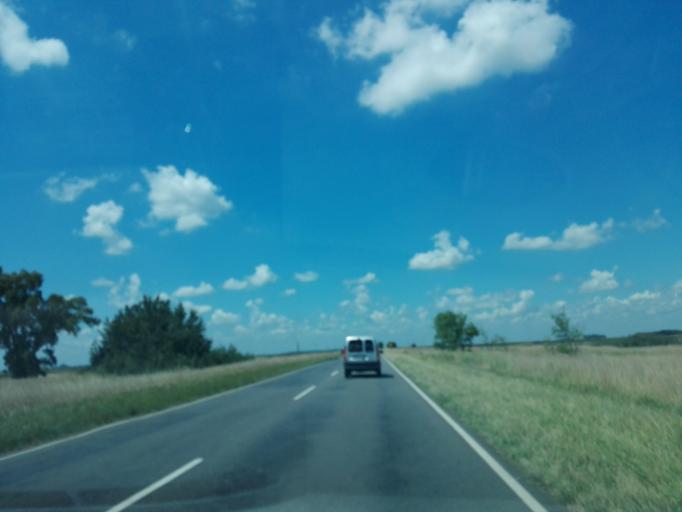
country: AR
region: Buenos Aires
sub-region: Partido de General Belgrano
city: General Belgrano
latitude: -35.9342
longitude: -58.6200
